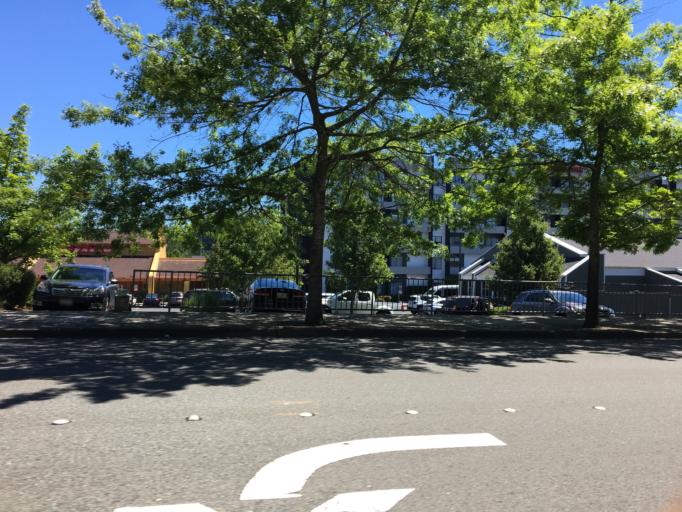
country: US
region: Washington
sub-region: King County
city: Bellevue
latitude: 47.6115
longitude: -122.1910
